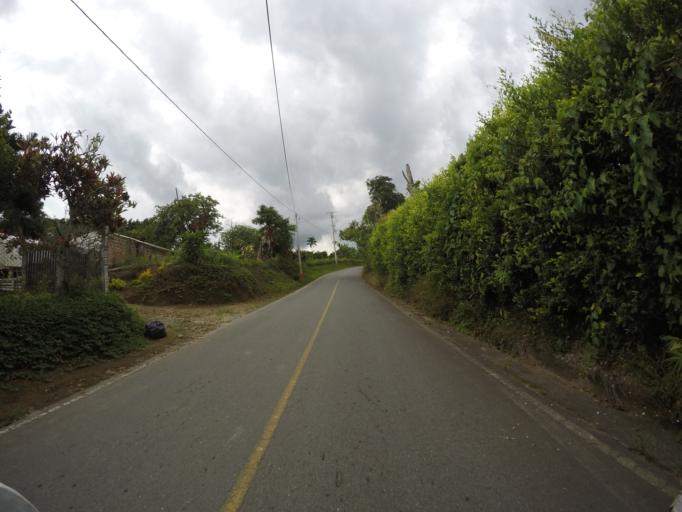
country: CO
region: Quindio
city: Quimbaya
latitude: 4.6069
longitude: -75.7310
